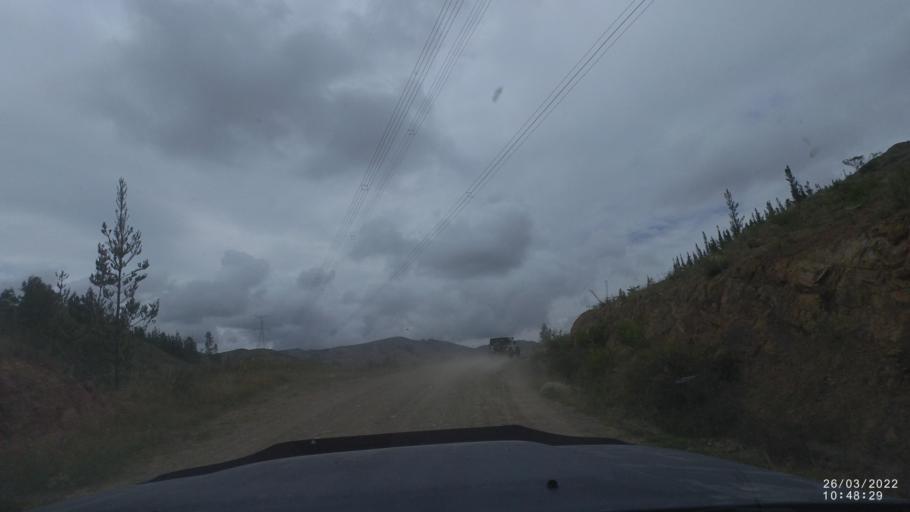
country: BO
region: Cochabamba
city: Tarata
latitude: -17.4959
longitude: -66.0438
